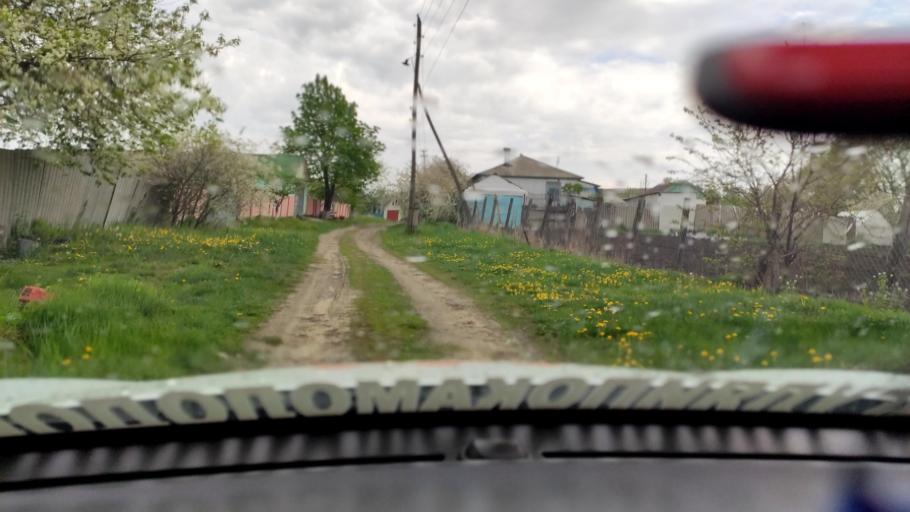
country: RU
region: Voronezj
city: Uryv-Pokrovka
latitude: 51.1199
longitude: 39.1701
